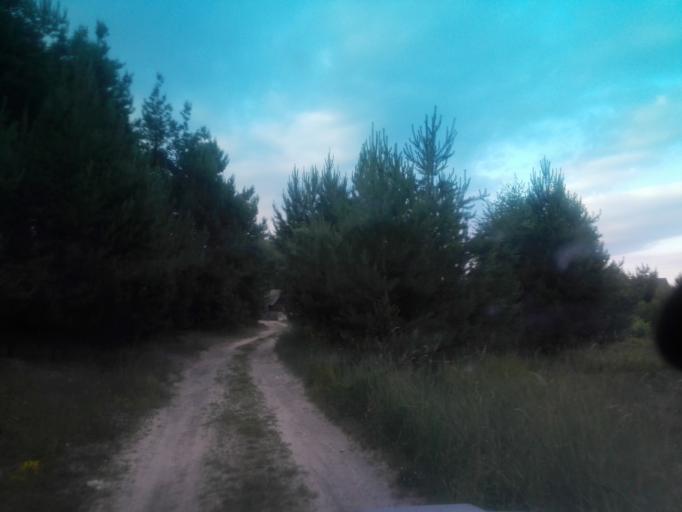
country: PL
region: Silesian Voivodeship
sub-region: Powiat czestochowski
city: Potok Zloty
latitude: 50.6917
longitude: 19.3733
